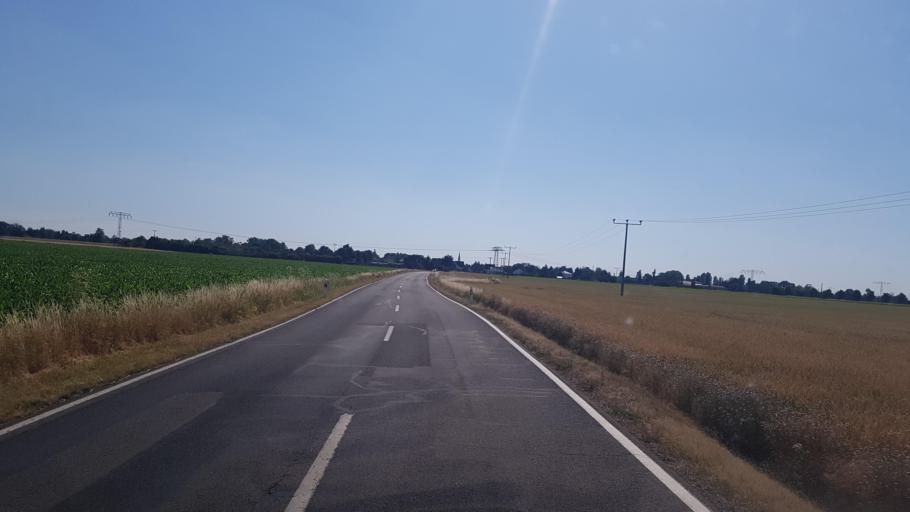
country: DE
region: Saxony-Anhalt
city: Prettin
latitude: 51.6689
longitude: 12.9495
